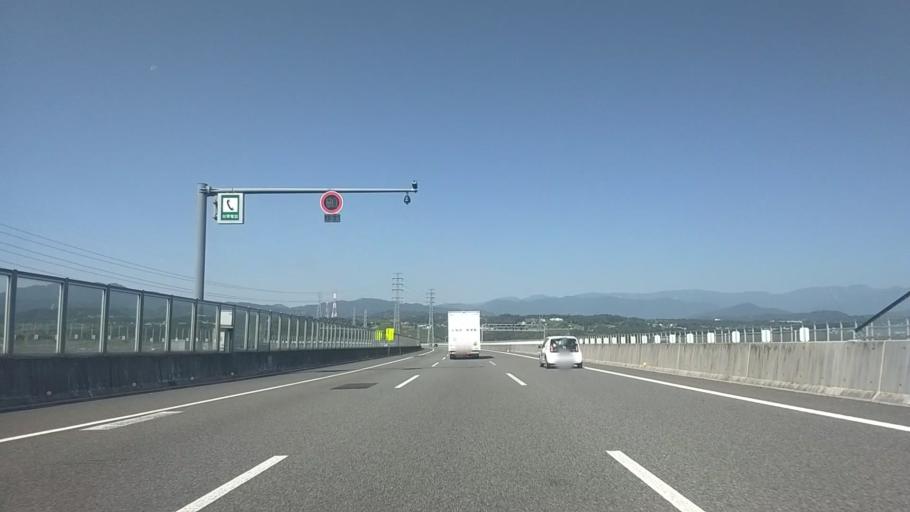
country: JP
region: Shizuoka
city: Fujinomiya
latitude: 35.2009
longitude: 138.6538
